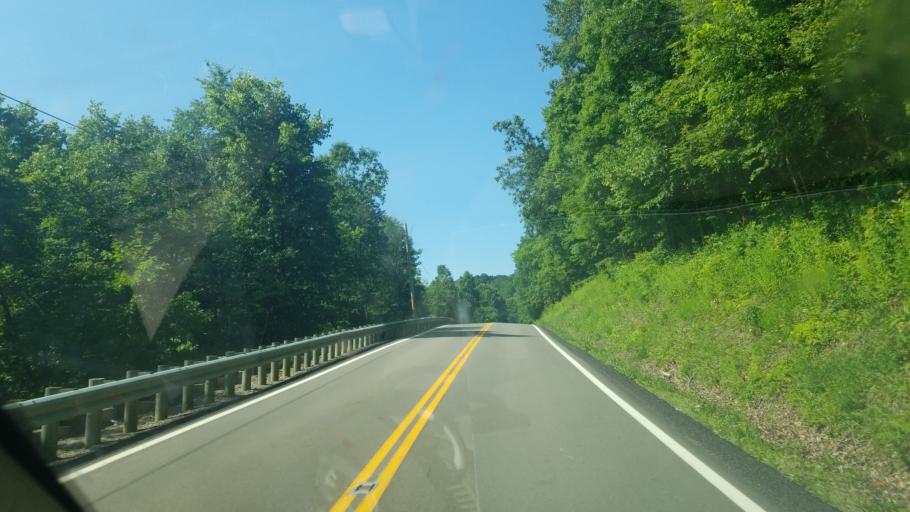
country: US
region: Ohio
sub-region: Holmes County
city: Millersburg
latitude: 40.4668
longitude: -81.9781
